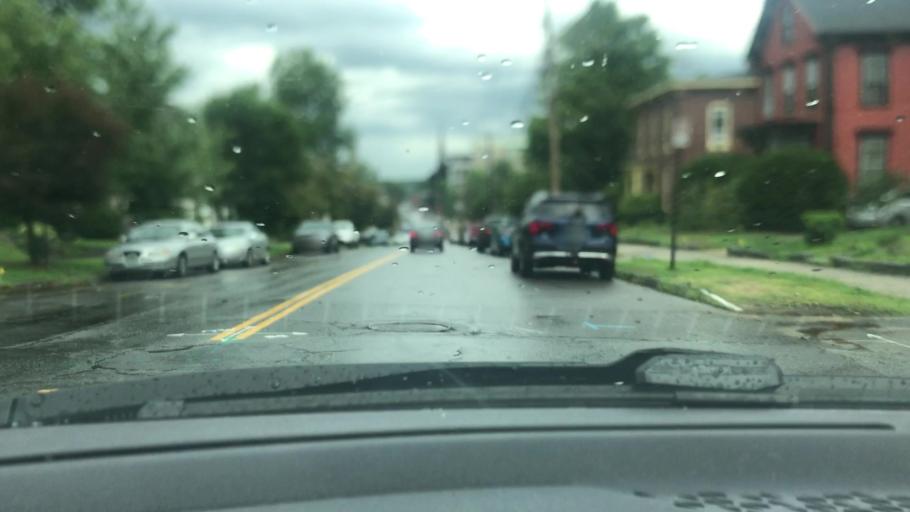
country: US
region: New Hampshire
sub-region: Merrimack County
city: Concord
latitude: 43.2010
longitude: -71.5429
